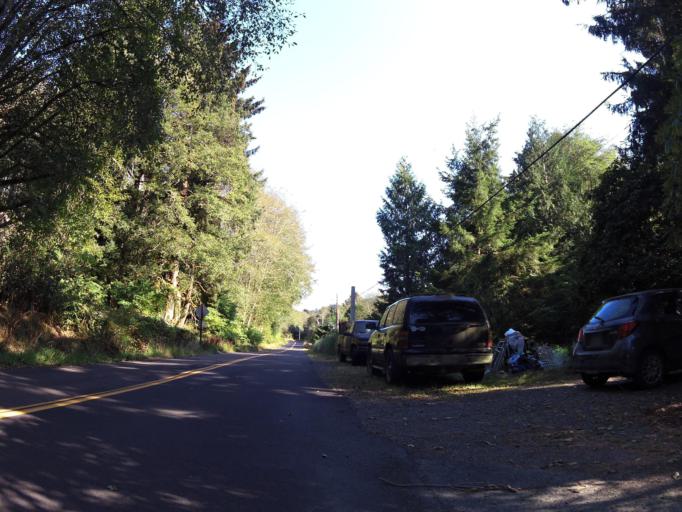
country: US
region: Oregon
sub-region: Lincoln County
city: Rose Lodge
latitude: 45.0793
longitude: -123.9407
